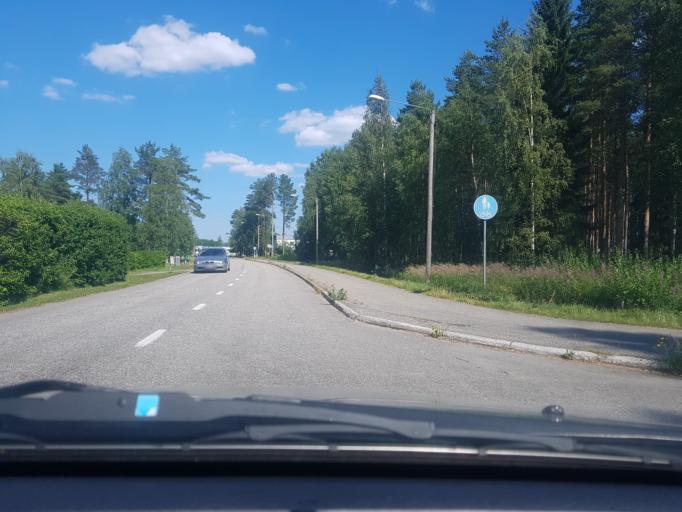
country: FI
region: Kainuu
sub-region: Kehys-Kainuu
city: Kuhmo
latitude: 64.1218
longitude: 29.5324
